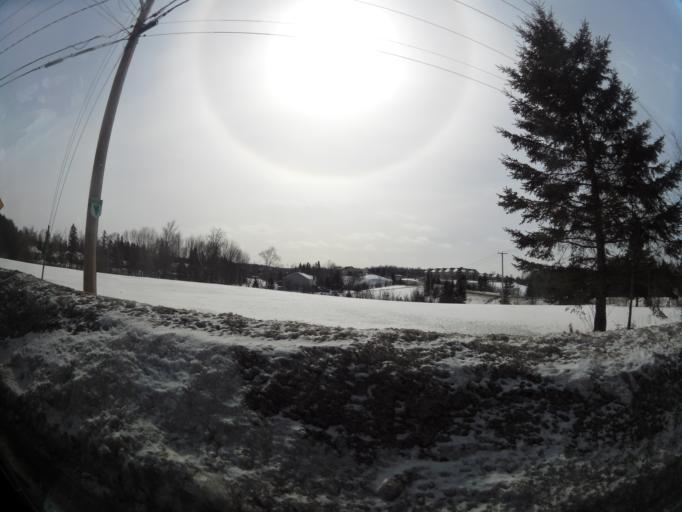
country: CA
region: Quebec
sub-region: Laurentides
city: Mont-Laurier
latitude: 46.5560
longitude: -75.5141
